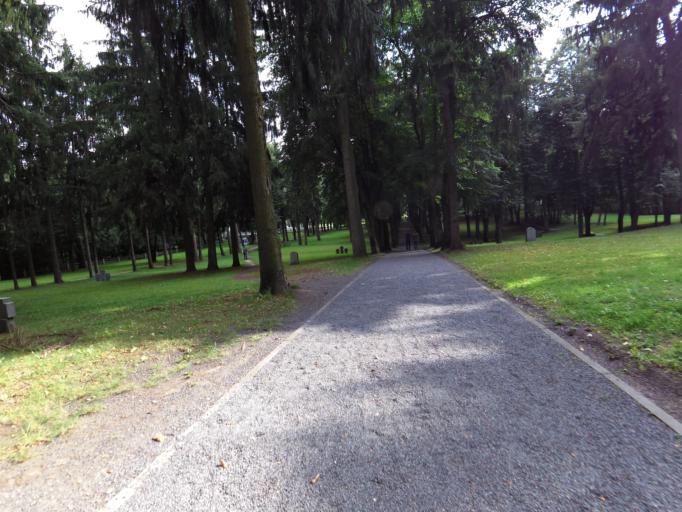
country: LT
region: Vilnius County
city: Vilkpede
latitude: 54.6838
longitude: 25.2482
